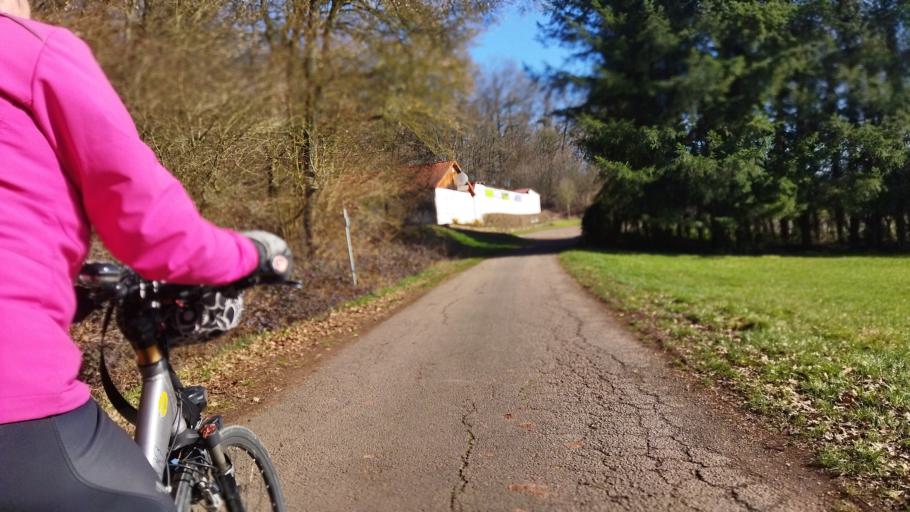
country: DE
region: Rheinland-Pfalz
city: Rehweiler
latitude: 49.4901
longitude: 7.4423
